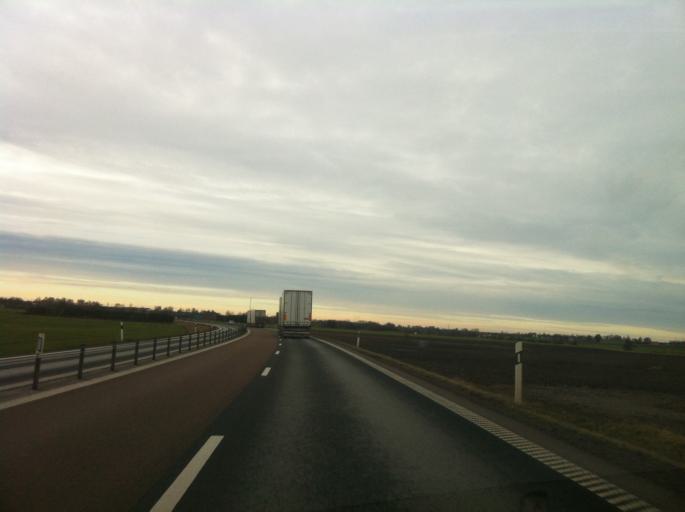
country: SE
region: Skane
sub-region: Astorps Kommun
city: Astorp
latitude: 56.1367
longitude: 12.9844
